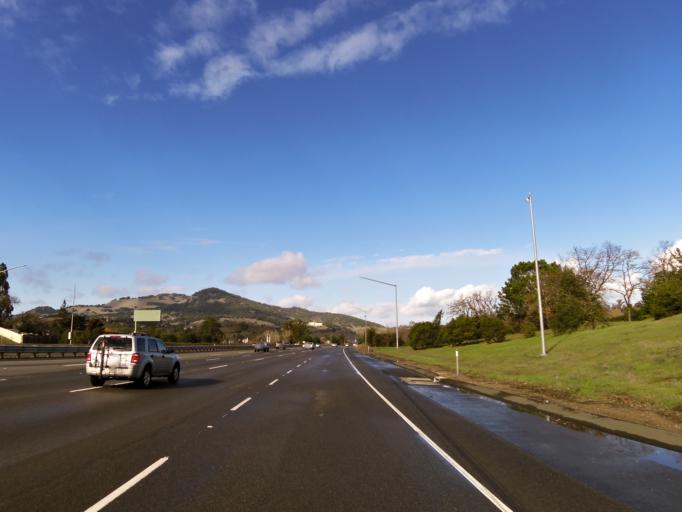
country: US
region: California
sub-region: Marin County
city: Novato
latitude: 38.1076
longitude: -122.5630
